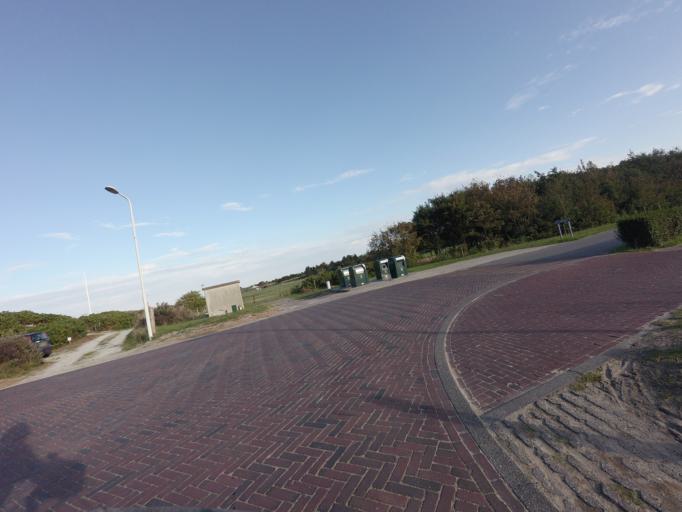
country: NL
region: Friesland
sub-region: Gemeente Ameland
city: Nes
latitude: 53.4564
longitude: 5.8044
